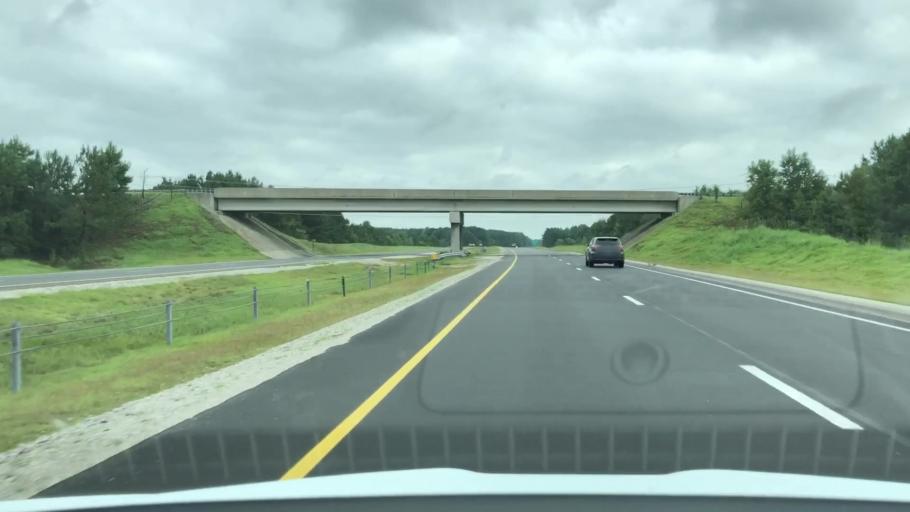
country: US
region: North Carolina
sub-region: Wilson County
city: Lucama
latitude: 35.6451
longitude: -77.9635
